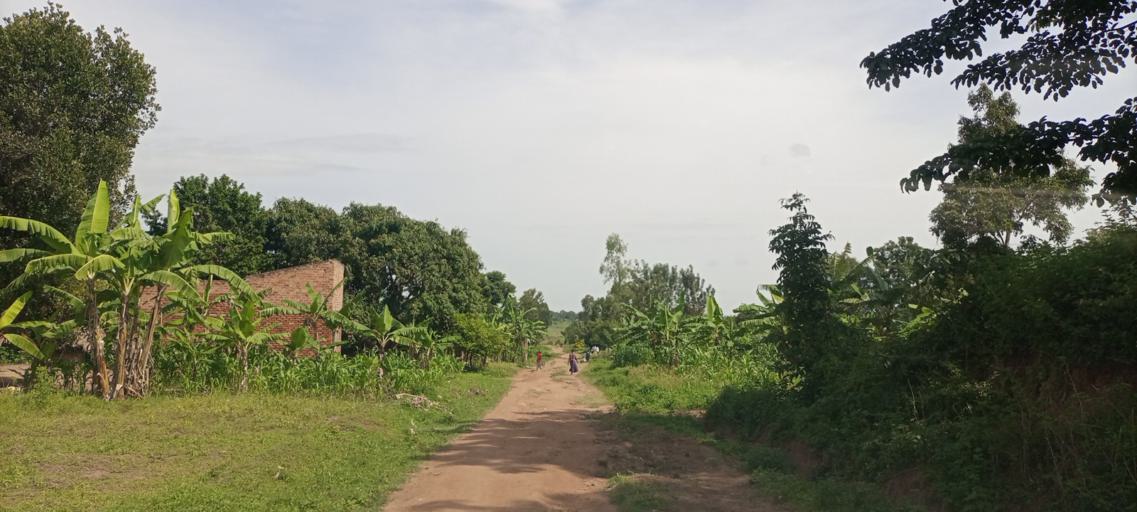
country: UG
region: Eastern Region
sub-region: Budaka District
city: Budaka
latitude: 1.1364
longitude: 34.0154
